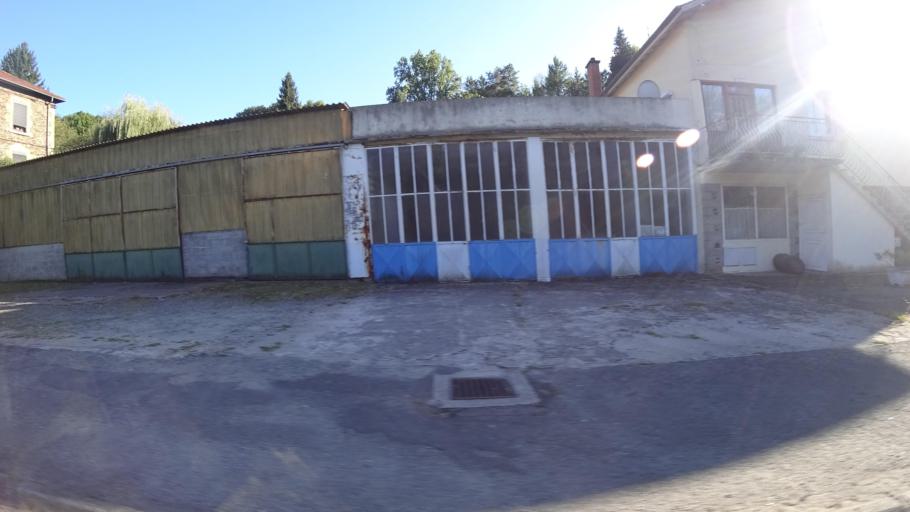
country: FR
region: Midi-Pyrenees
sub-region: Departement de l'Aveyron
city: Cransac
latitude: 44.5239
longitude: 2.2888
